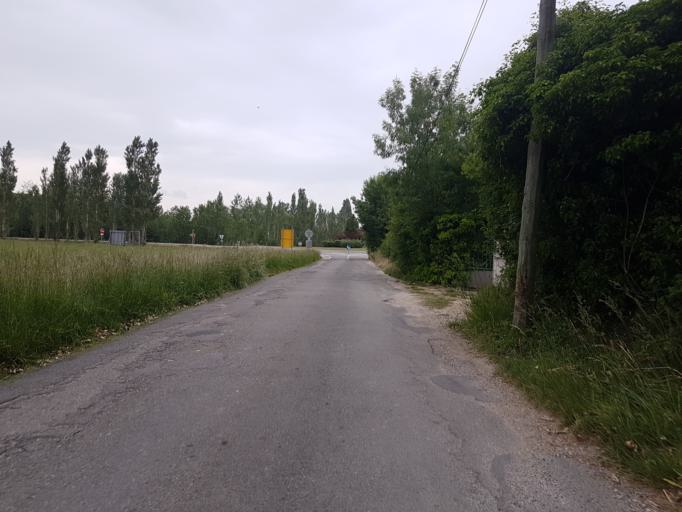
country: FR
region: Languedoc-Roussillon
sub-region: Departement du Gard
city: Roquemaure
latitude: 44.0574
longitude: 4.7771
